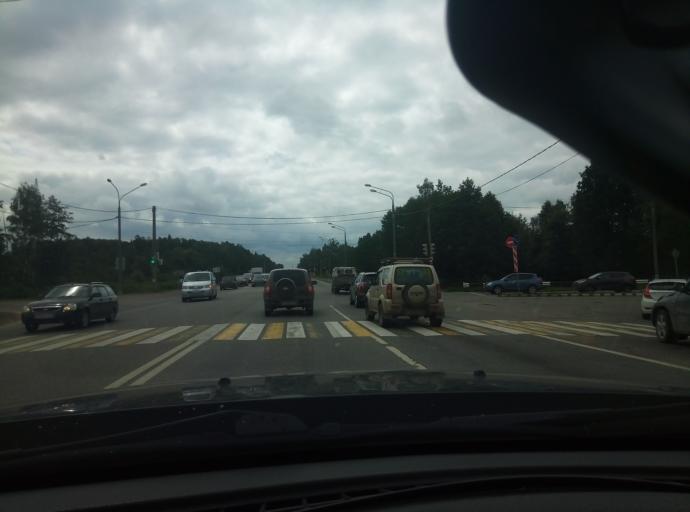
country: RU
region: Kaluga
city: Obninsk
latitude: 55.0891
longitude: 36.6339
